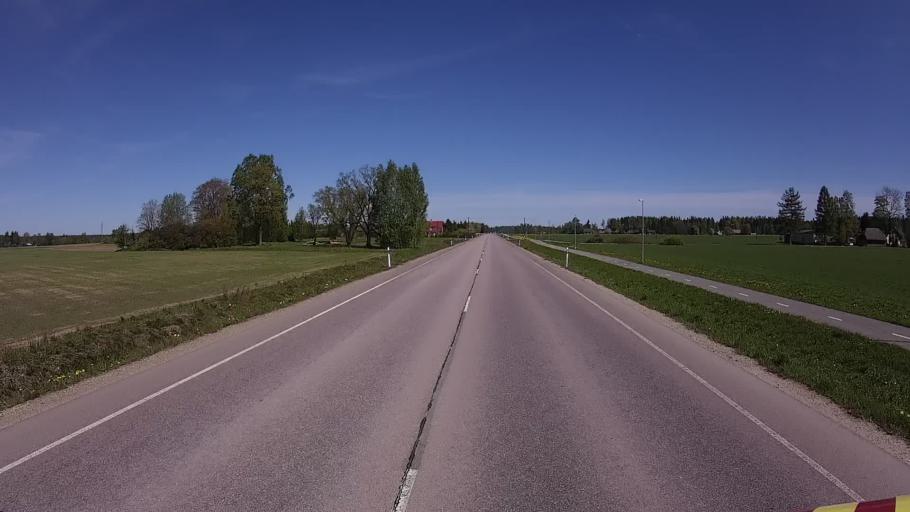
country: EE
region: Polvamaa
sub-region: Polva linn
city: Polva
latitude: 58.0784
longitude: 27.0892
